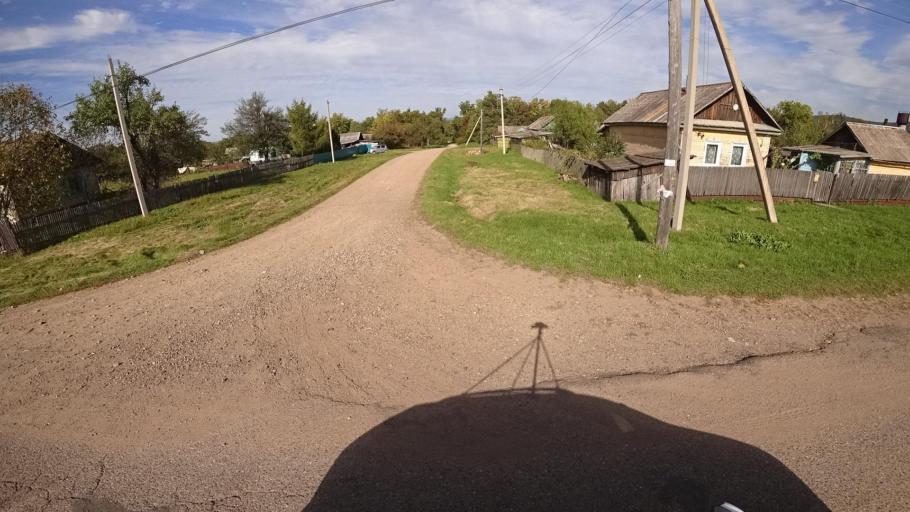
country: RU
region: Primorskiy
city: Dostoyevka
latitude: 44.2985
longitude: 133.4521
